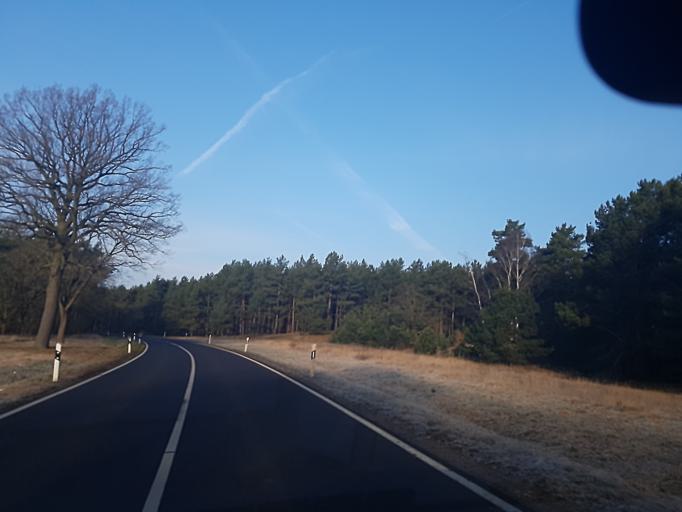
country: DE
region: Brandenburg
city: Golzow
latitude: 52.2782
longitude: 12.6180
